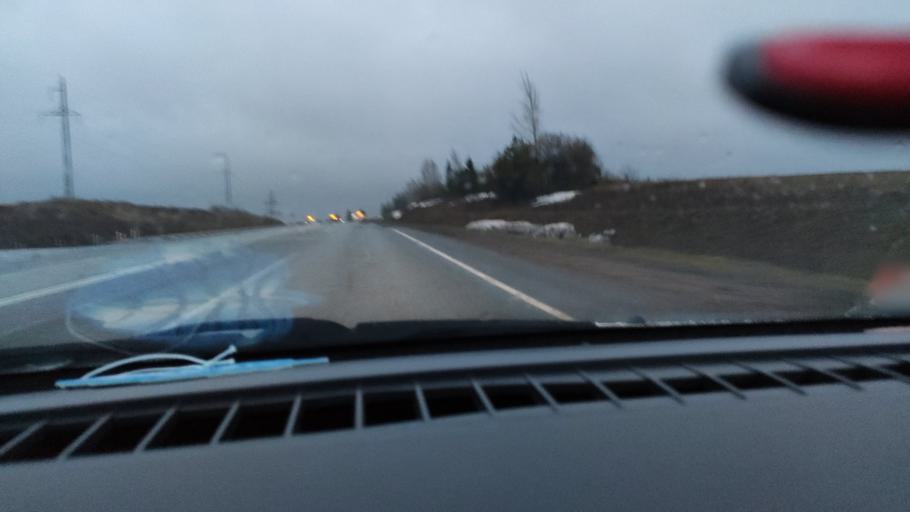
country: RU
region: Udmurtiya
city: Alnashi
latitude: 56.2580
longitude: 52.3753
